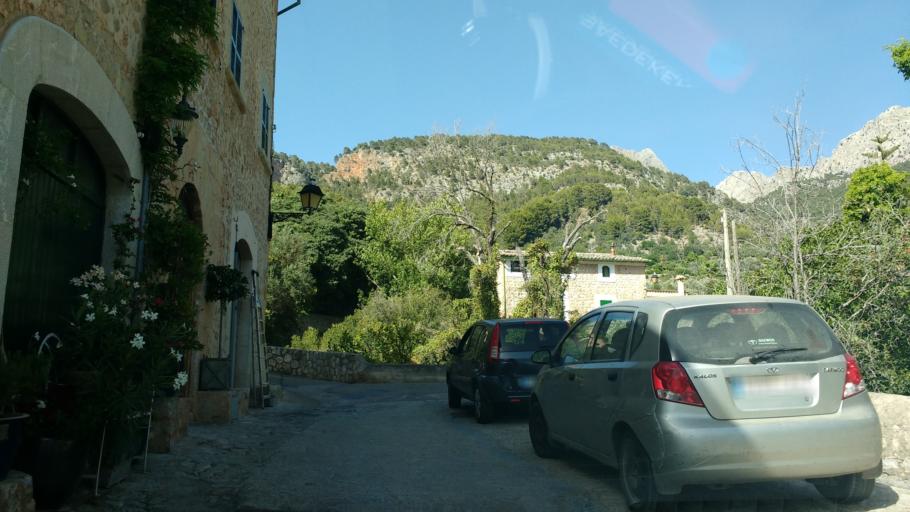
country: ES
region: Balearic Islands
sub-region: Illes Balears
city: Fornalutx
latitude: 39.7836
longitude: 2.7434
